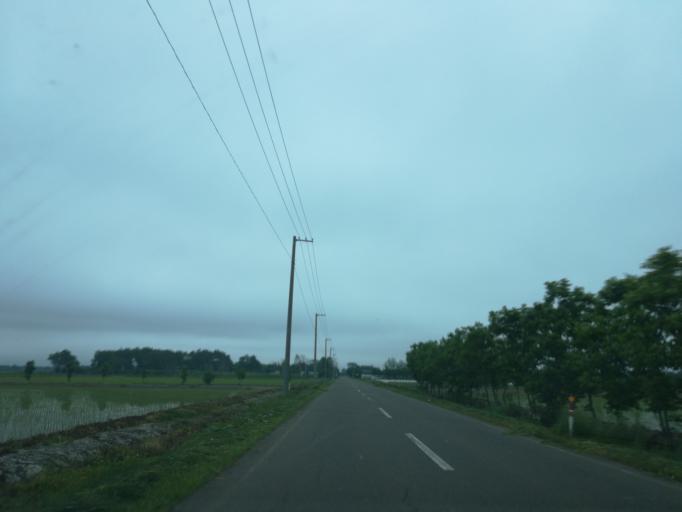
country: JP
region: Hokkaido
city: Ebetsu
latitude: 43.0682
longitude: 141.6383
